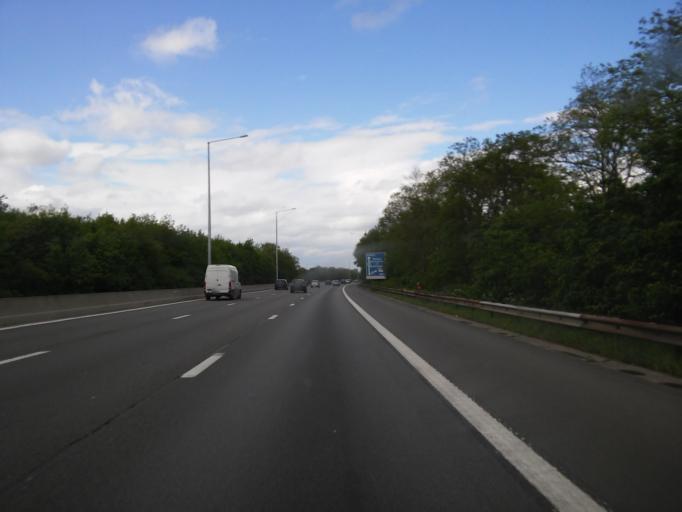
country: BE
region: Flanders
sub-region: Provincie Antwerpen
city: Mechelen
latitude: 51.0305
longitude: 4.4480
